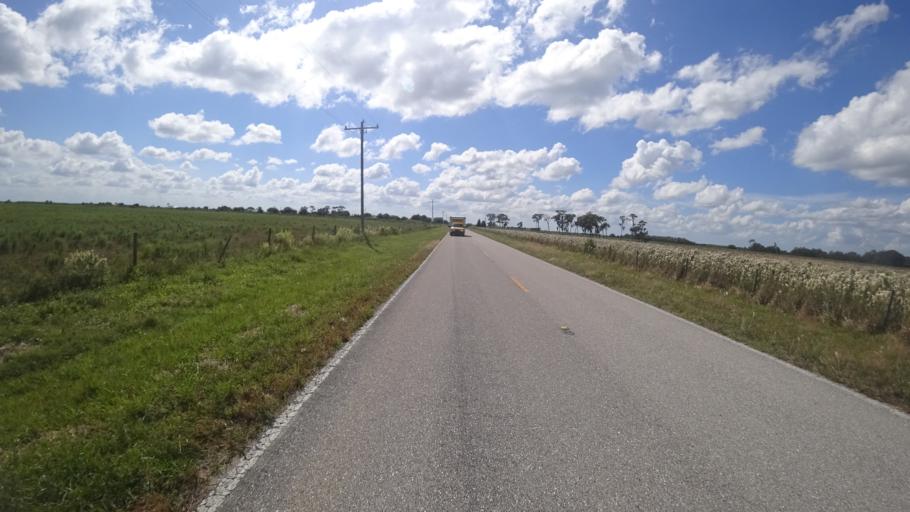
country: US
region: Florida
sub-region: Sarasota County
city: Lake Sarasota
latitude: 27.3079
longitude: -82.1830
